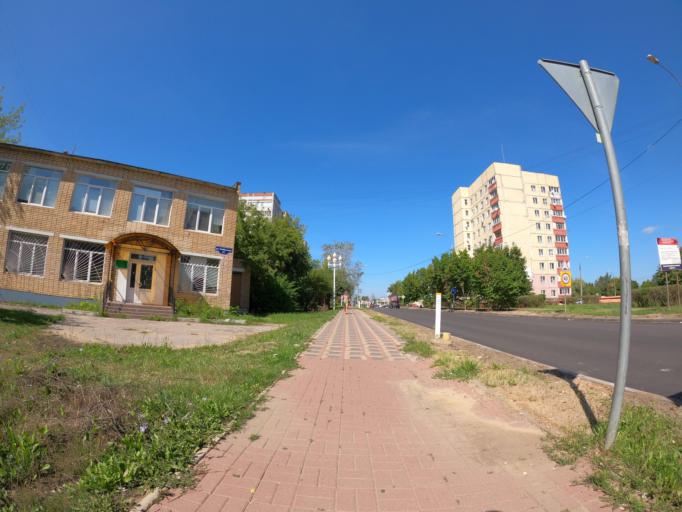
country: RU
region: Moskovskaya
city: Stupino
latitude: 54.8942
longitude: 38.0731
